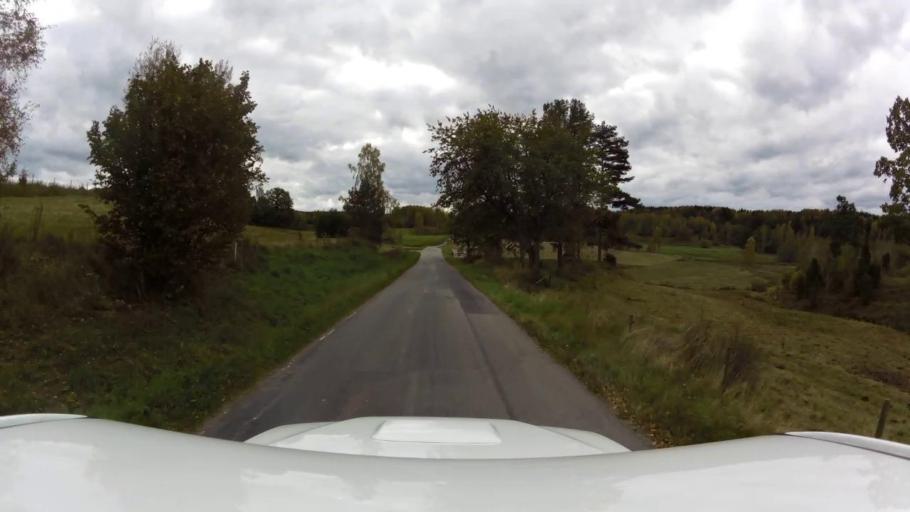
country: SE
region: OEstergoetland
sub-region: Kinda Kommun
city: Rimforsa
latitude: 58.1995
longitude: 15.5696
